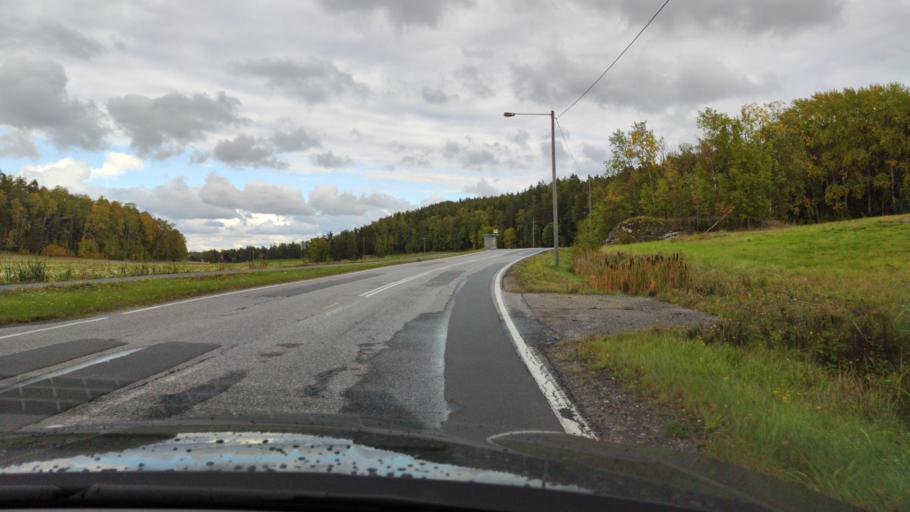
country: FI
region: Varsinais-Suomi
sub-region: Turku
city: Turku
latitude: 60.3616
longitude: 22.1868
